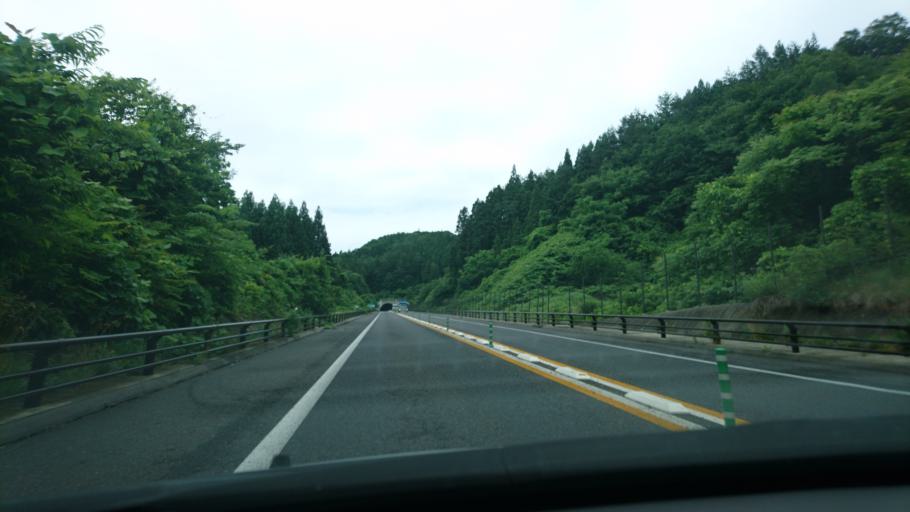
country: JP
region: Iwate
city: Miyako
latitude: 40.0133
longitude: 141.8871
